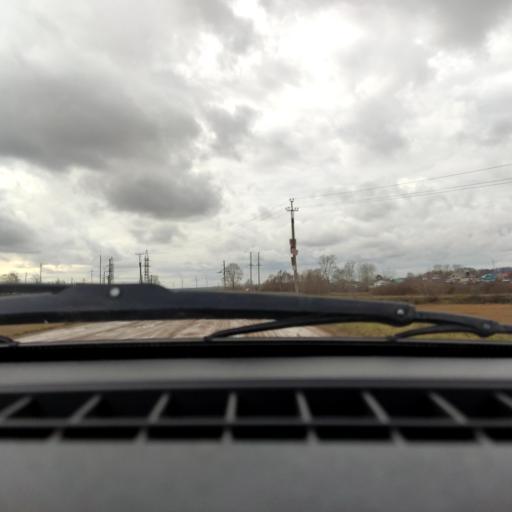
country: RU
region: Bashkortostan
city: Asanovo
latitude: 54.9577
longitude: 55.5646
